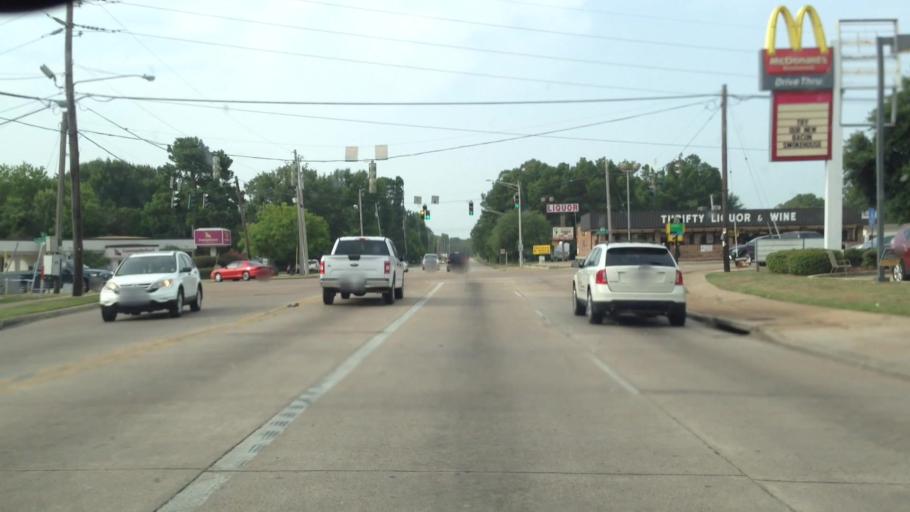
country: US
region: Louisiana
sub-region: De Soto Parish
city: Stonewall
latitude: 32.4027
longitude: -93.8147
